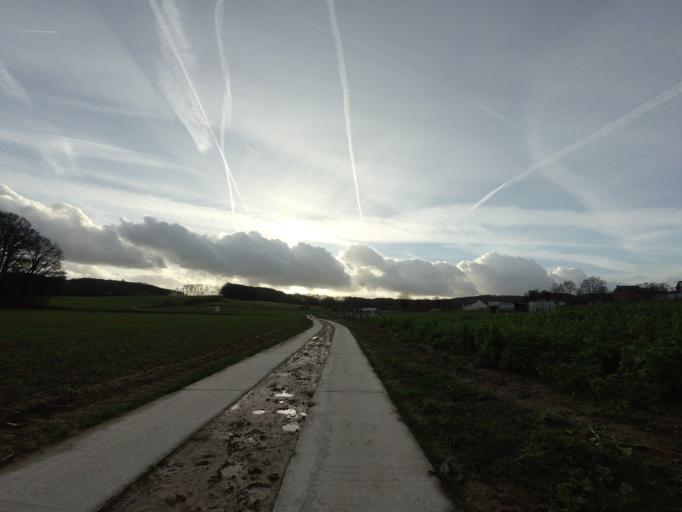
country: BE
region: Flanders
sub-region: Provincie Vlaams-Brabant
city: Kortenberg
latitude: 50.8725
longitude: 4.5721
